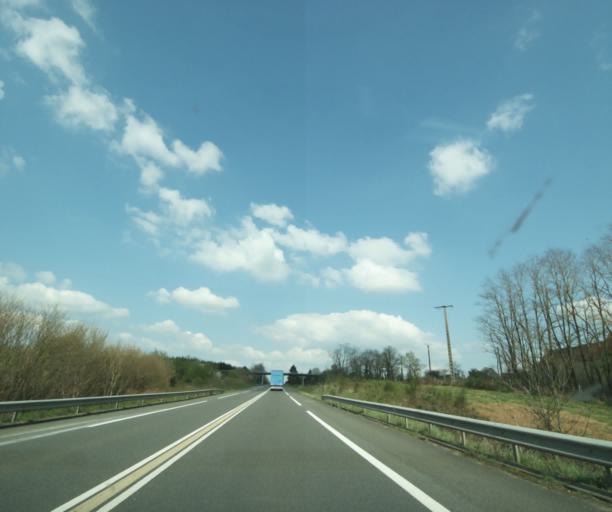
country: FR
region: Auvergne
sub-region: Departement de l'Allier
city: Montmarault
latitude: 46.3417
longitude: 2.9860
